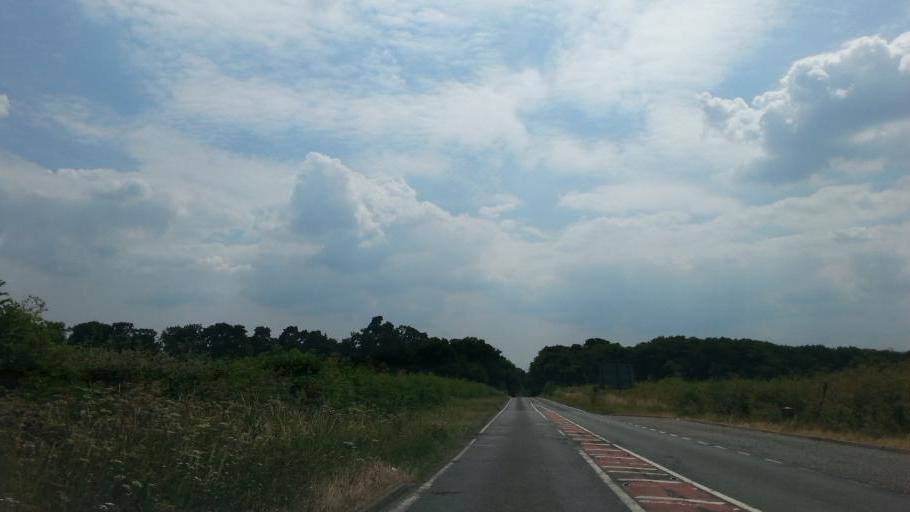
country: GB
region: England
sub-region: Suffolk
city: Lakenheath
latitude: 52.3683
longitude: 0.5403
